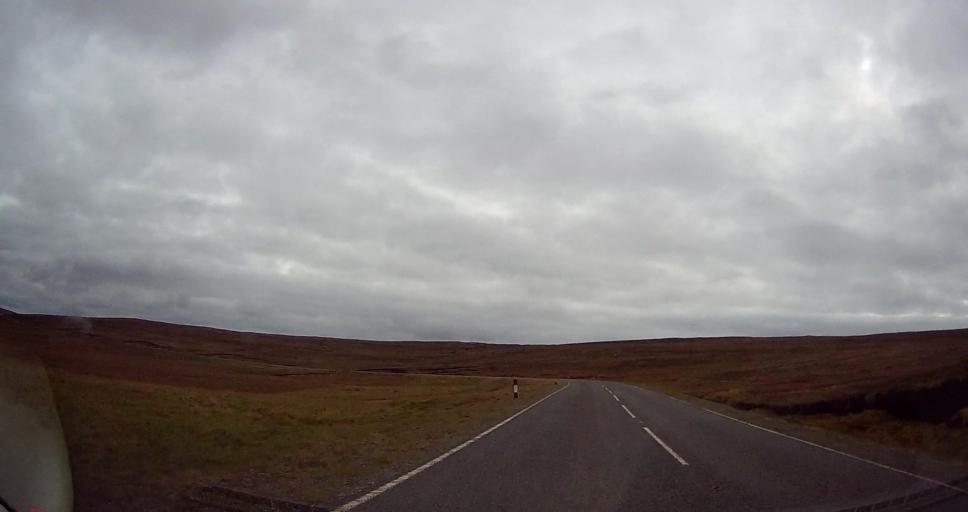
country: GB
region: Scotland
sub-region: Shetland Islands
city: Shetland
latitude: 60.6475
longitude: -1.0686
